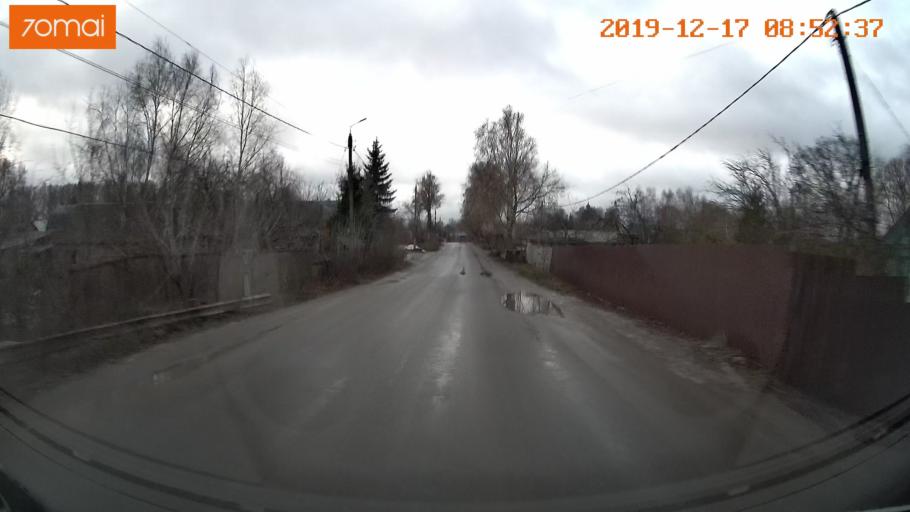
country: RU
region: Vladimir
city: Kosterevo
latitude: 55.9470
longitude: 39.6323
